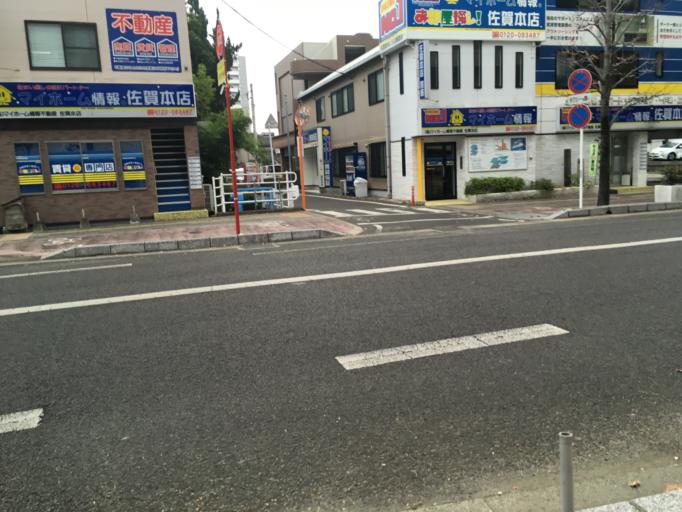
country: JP
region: Saga Prefecture
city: Saga-shi
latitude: 33.2617
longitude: 130.2971
